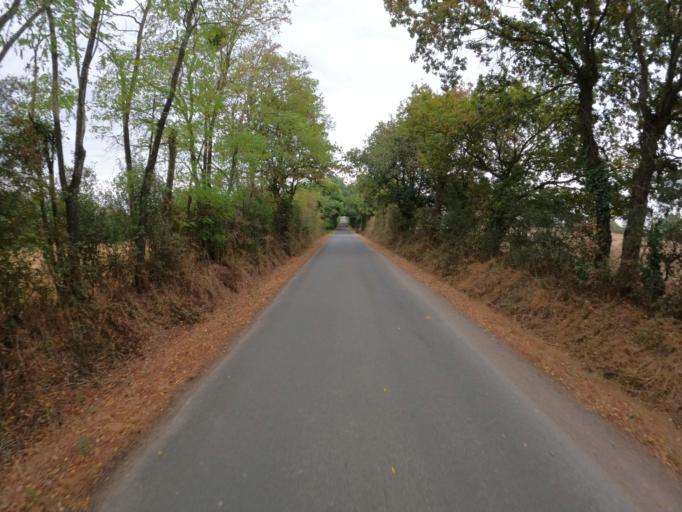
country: FR
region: Pays de la Loire
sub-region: Departement de la Vendee
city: La Boissiere-de-Montaigu
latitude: 46.9854
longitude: -1.1650
